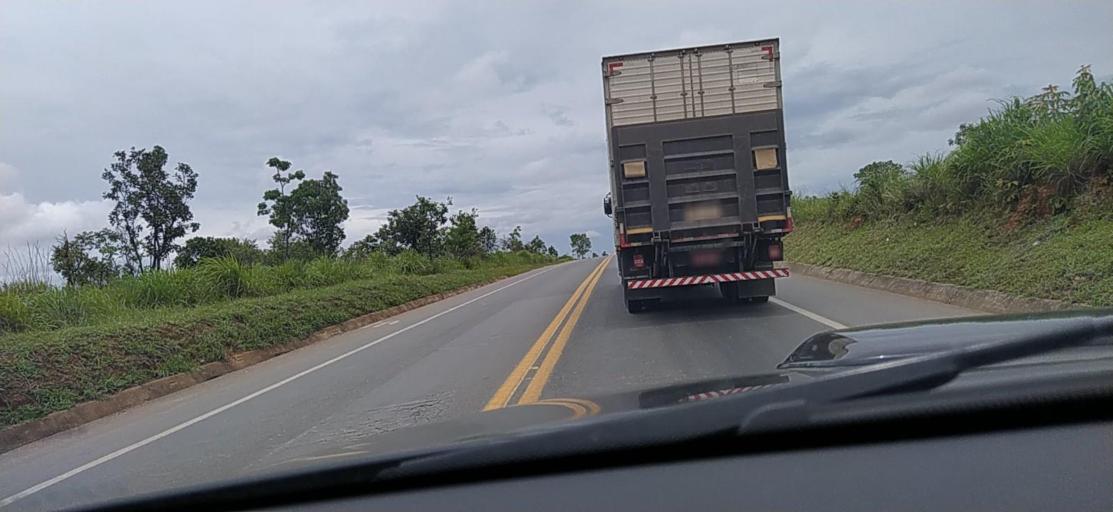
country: BR
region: Minas Gerais
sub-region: Curvelo
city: Curvelo
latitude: -18.7311
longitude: -44.4426
